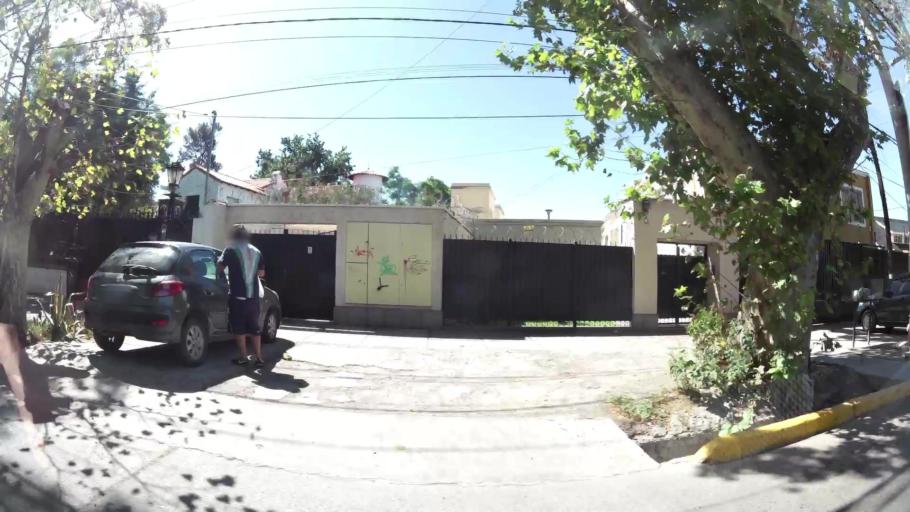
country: AR
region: Mendoza
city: Mendoza
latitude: -32.8969
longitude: -68.8050
